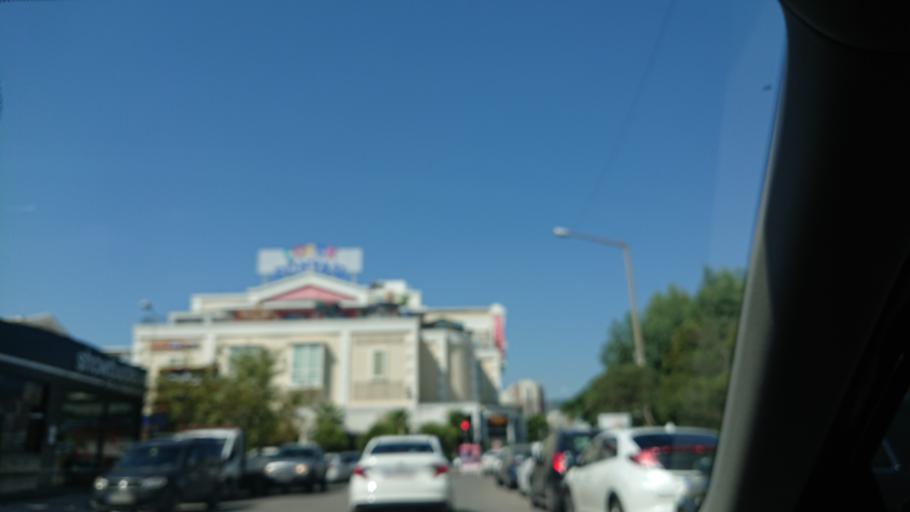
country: TR
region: Izmir
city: Karsiyaka
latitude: 38.4718
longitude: 27.0755
